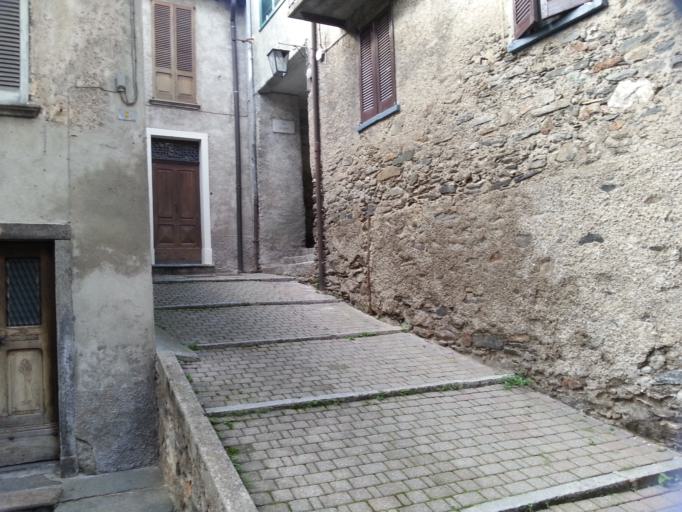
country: IT
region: Lombardy
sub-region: Provincia di Lecco
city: Premana
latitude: 46.0516
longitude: 9.4241
